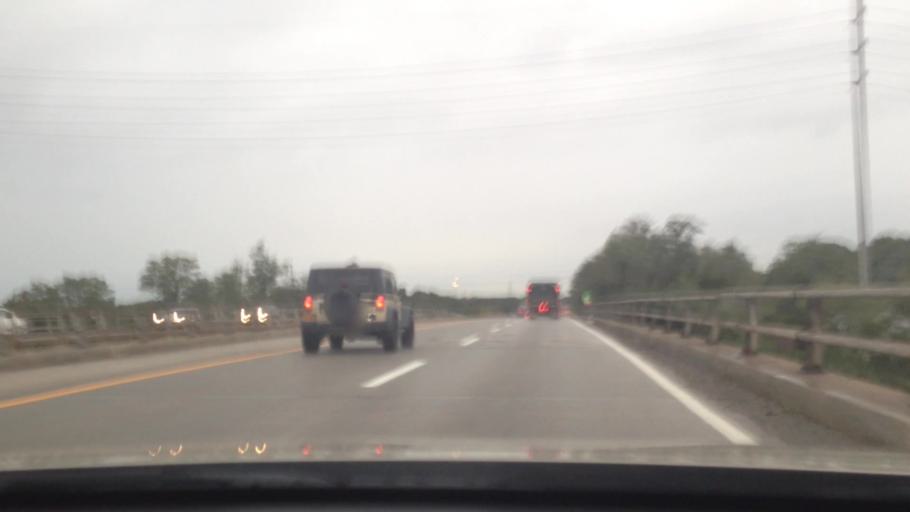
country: US
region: New York
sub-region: Suffolk County
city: Holtsville
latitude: 40.8123
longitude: -73.0530
